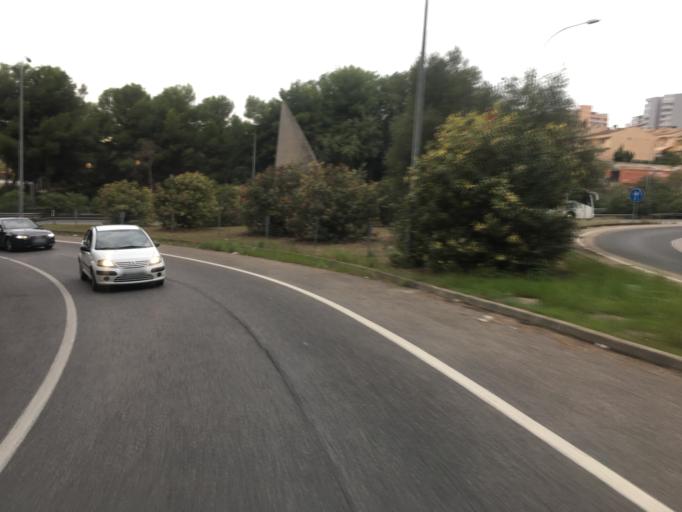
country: ES
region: Balearic Islands
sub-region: Illes Balears
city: Palma
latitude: 39.5541
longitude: 2.6158
